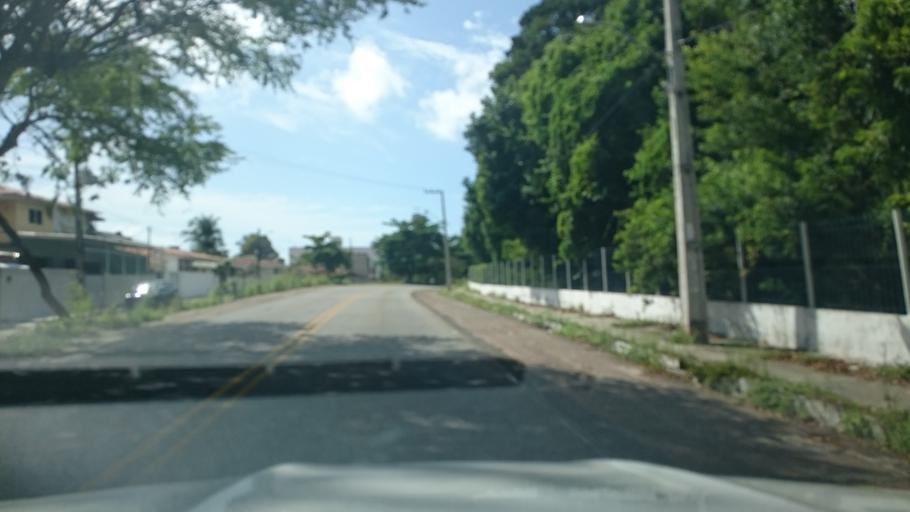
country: BR
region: Paraiba
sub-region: Joao Pessoa
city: Joao Pessoa
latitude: -7.1320
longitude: -34.8434
